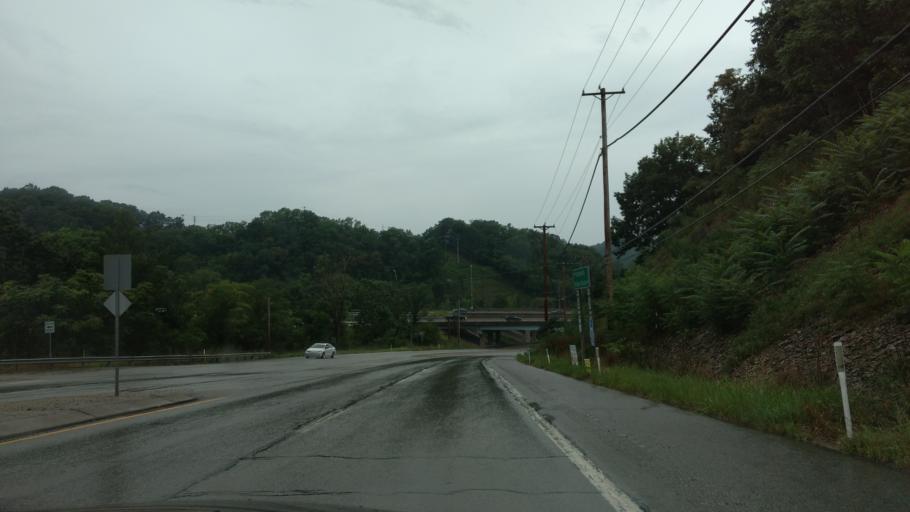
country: US
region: Pennsylvania
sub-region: Allegheny County
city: Coraopolis
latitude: 40.5040
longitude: -80.1348
